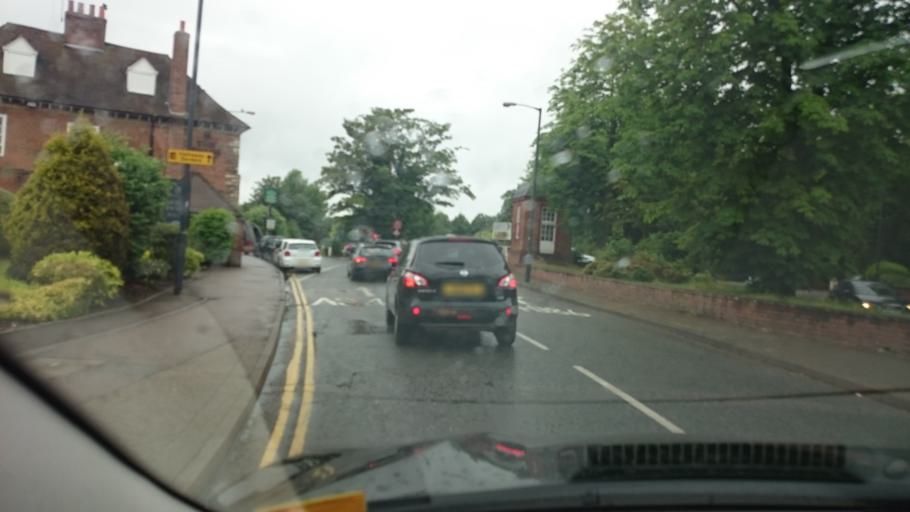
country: GB
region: England
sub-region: Warwickshire
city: Stratford-upon-Avon
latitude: 52.1906
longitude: -1.6989
